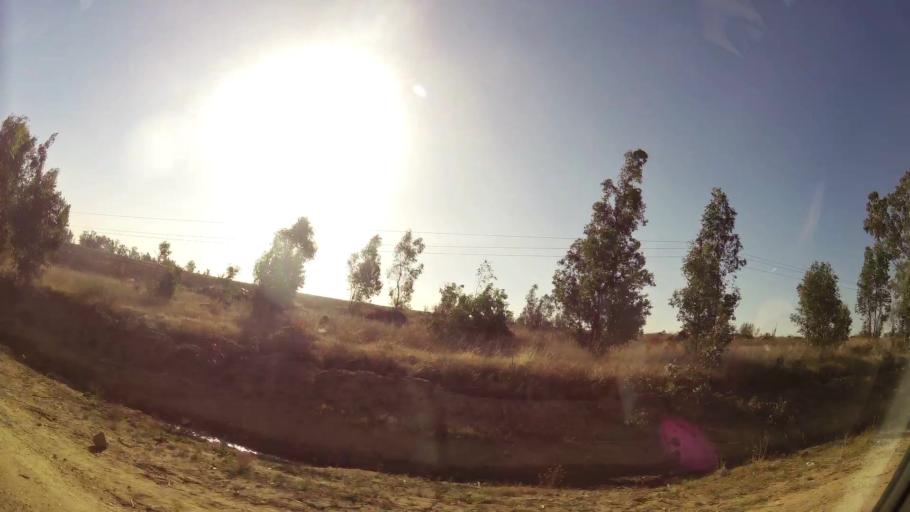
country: ZA
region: Gauteng
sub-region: City of Johannesburg Metropolitan Municipality
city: Diepsloot
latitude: -25.9474
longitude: 27.9683
